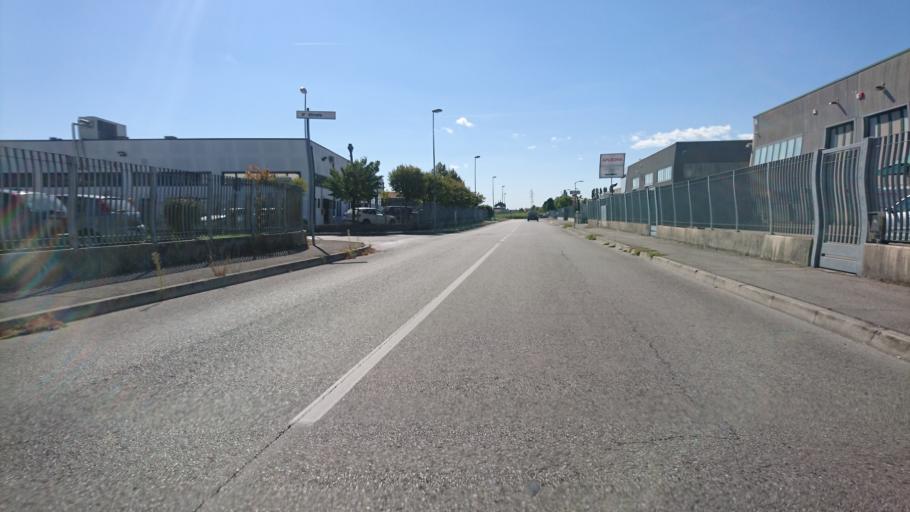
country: IT
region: Veneto
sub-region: Provincia di Venezia
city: Fosso
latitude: 45.3970
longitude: 12.0449
